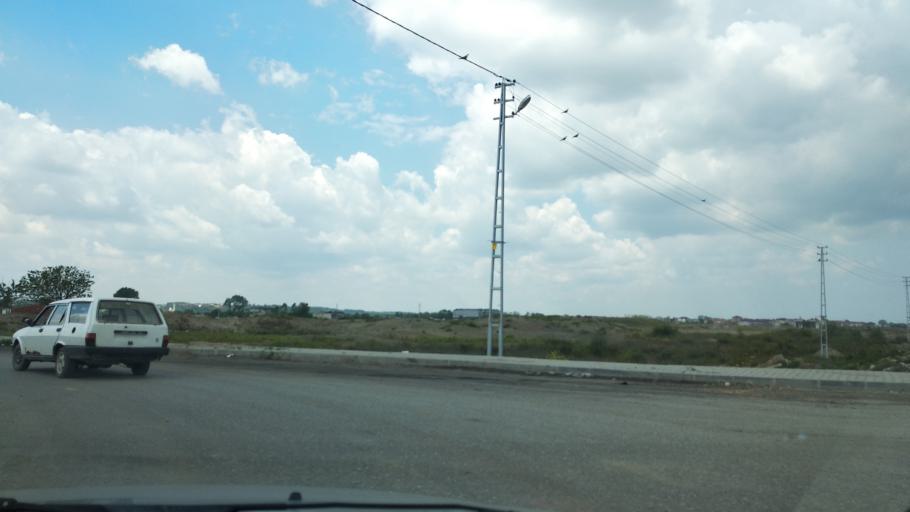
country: TR
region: Sakarya
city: Karasu
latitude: 41.1188
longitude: 30.6688
